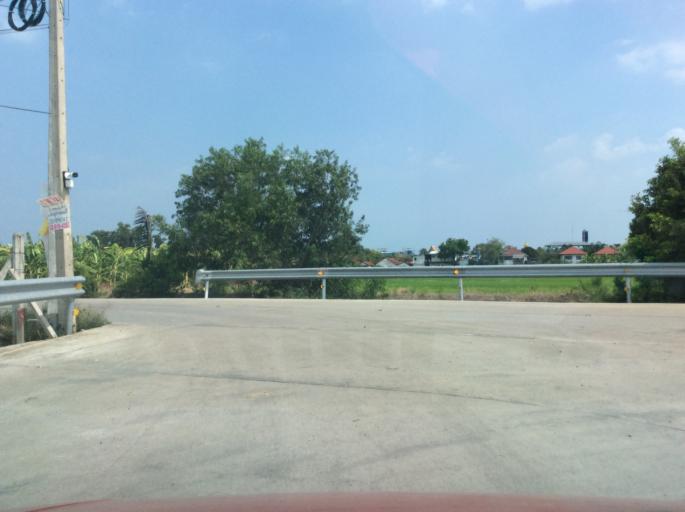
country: TH
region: Pathum Thani
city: Lam Luk Ka
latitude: 13.9394
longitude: 100.7241
